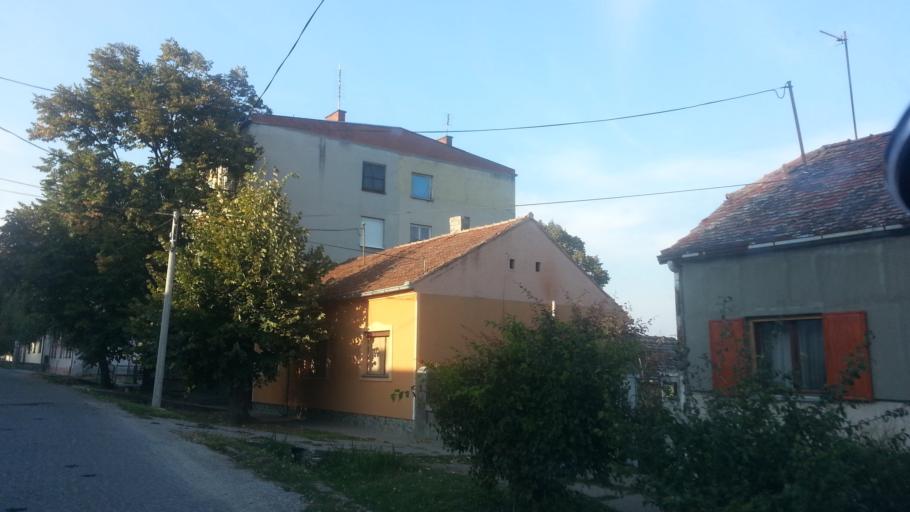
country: RS
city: Novi Slankamen
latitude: 45.1406
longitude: 20.2594
